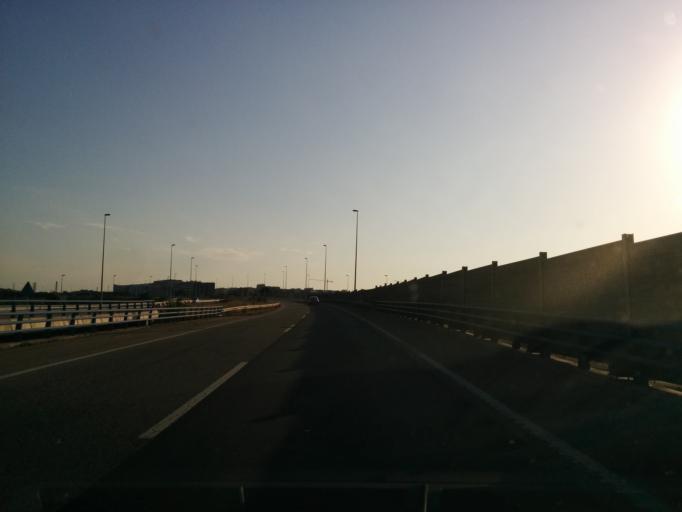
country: ES
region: Aragon
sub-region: Provincia de Zaragoza
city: Zaragoza
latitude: 41.6210
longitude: -0.8617
